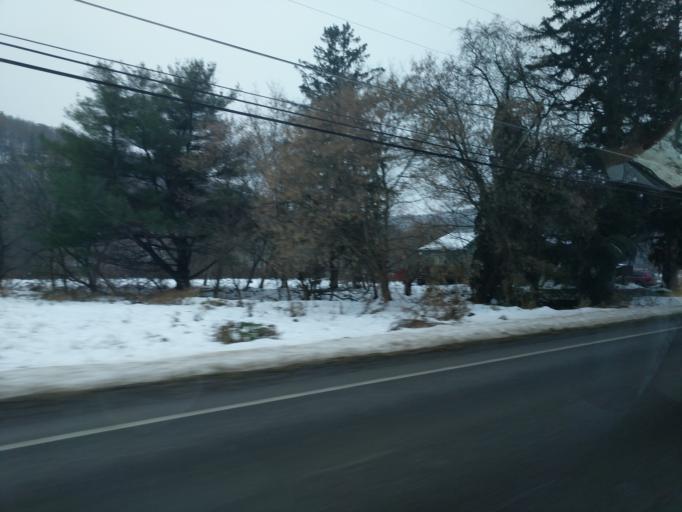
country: US
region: Pennsylvania
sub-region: Tioga County
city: Wellsboro
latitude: 41.8386
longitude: -77.2800
